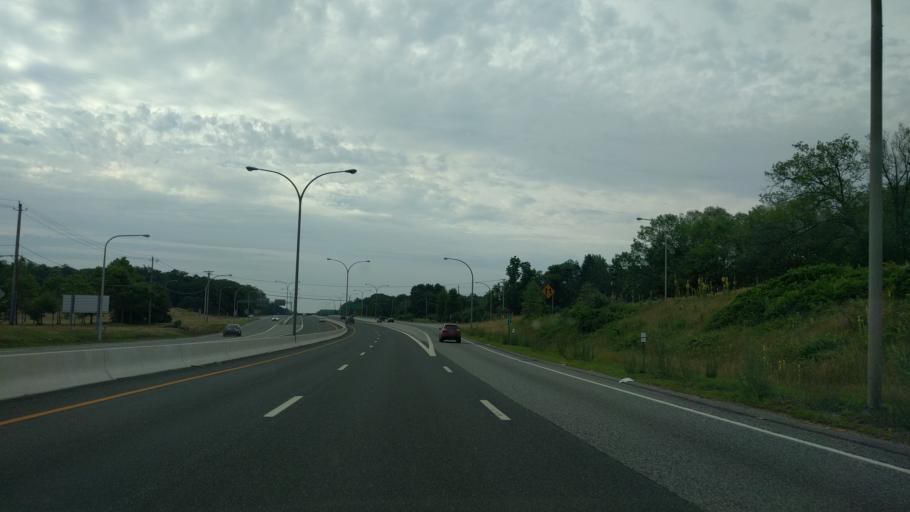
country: US
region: Rhode Island
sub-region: Providence County
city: Cumberland Hill
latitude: 41.9496
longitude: -71.4841
